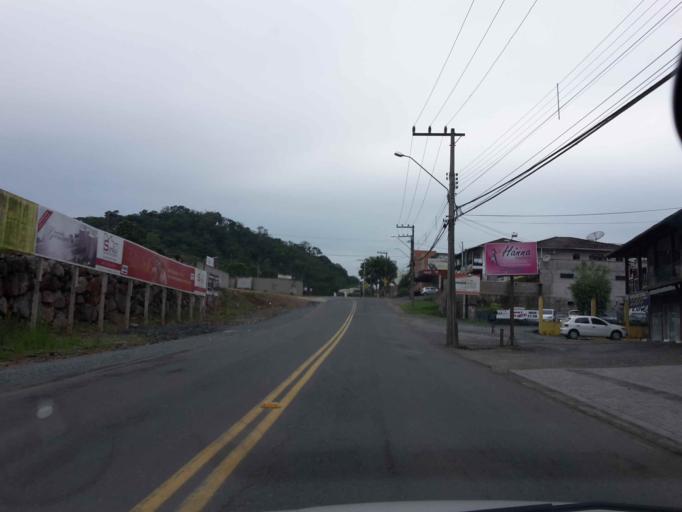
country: BR
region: Santa Catarina
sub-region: Blumenau
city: Blumenau
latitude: -26.8571
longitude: -49.1095
